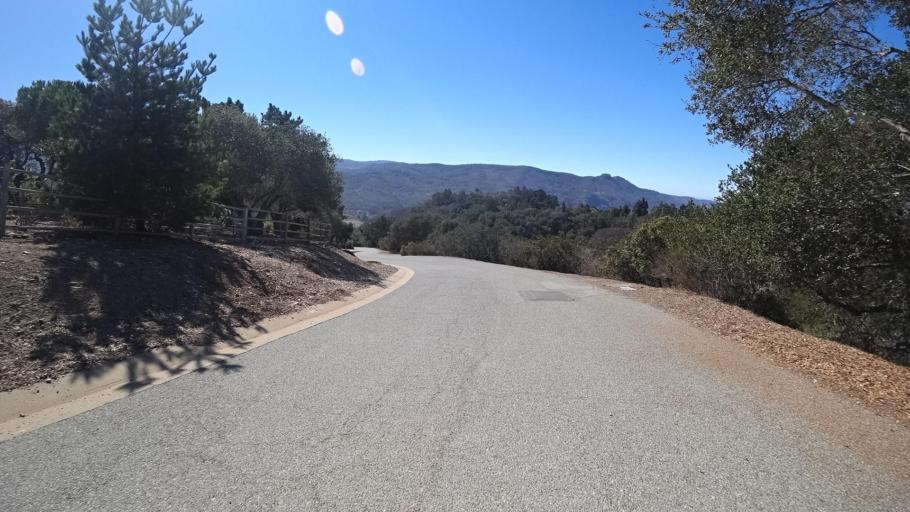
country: US
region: California
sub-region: Monterey County
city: Carmel Valley Village
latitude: 36.5301
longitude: -121.8073
